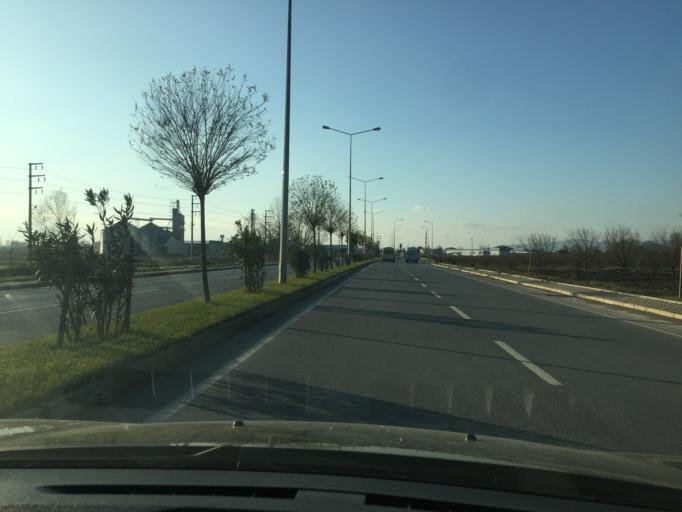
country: TR
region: Sakarya
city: Sogutlu
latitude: 40.9042
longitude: 30.4902
